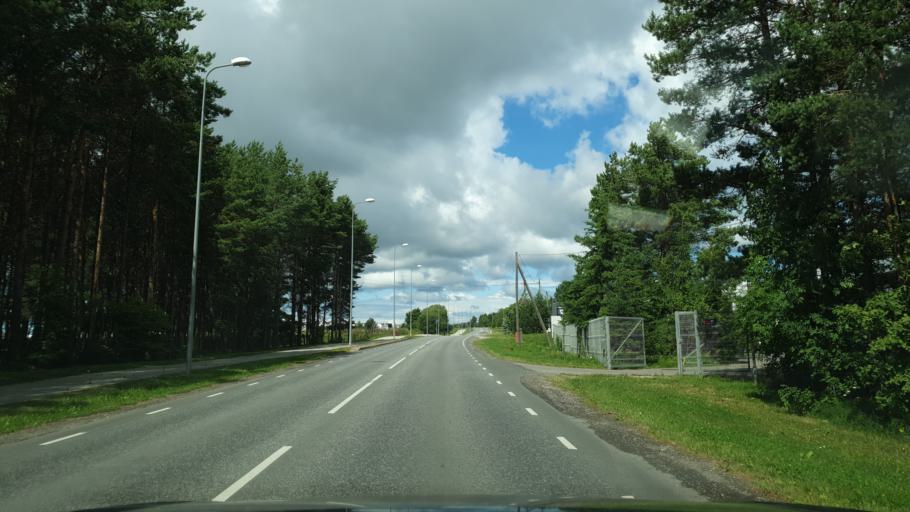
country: EE
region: Harju
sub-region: Viimsi vald
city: Viimsi
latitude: 59.4963
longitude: 24.8743
